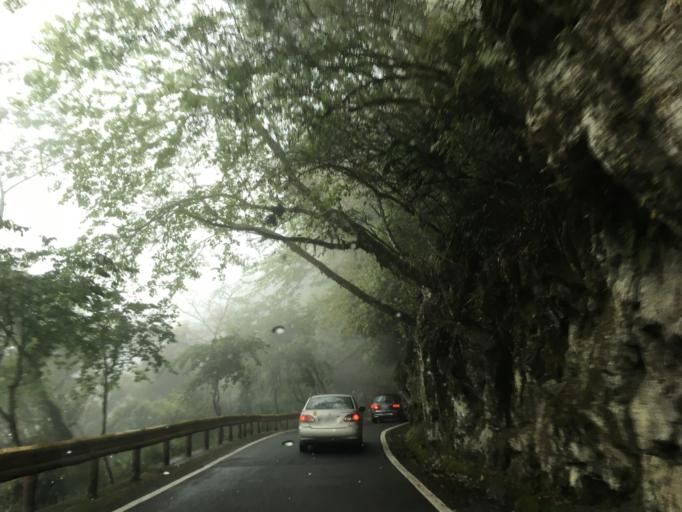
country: TW
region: Taiwan
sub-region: Hualien
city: Hualian
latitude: 24.1870
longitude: 121.4135
